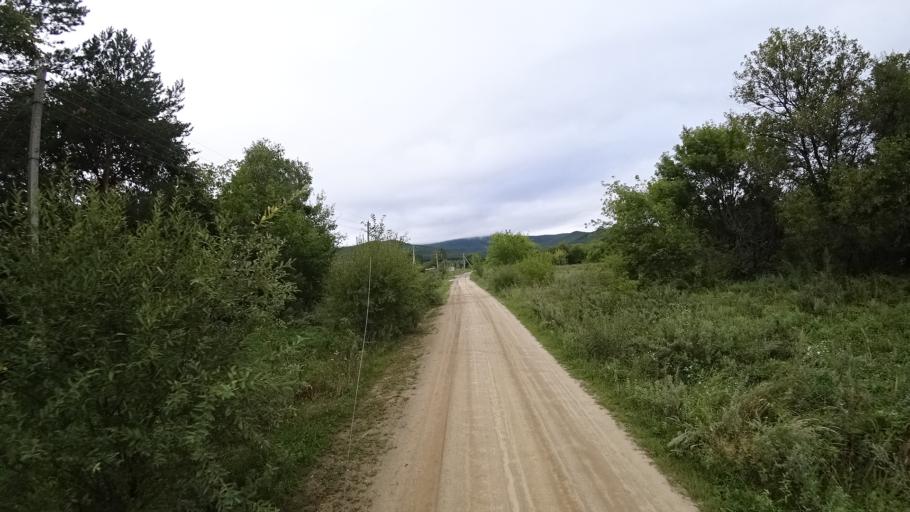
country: RU
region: Primorskiy
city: Rettikhovka
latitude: 44.1372
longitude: 132.6429
